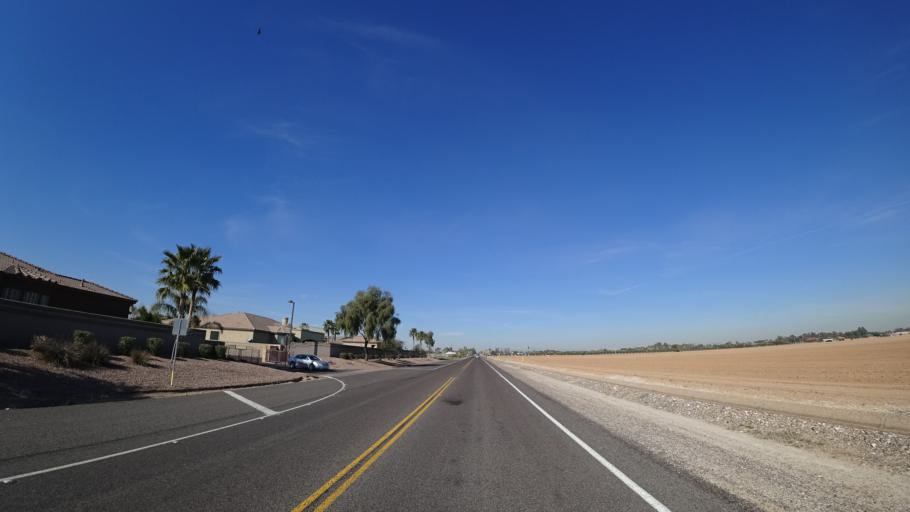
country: US
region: Arizona
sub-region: Maricopa County
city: Citrus Park
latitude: 33.5194
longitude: -112.4442
